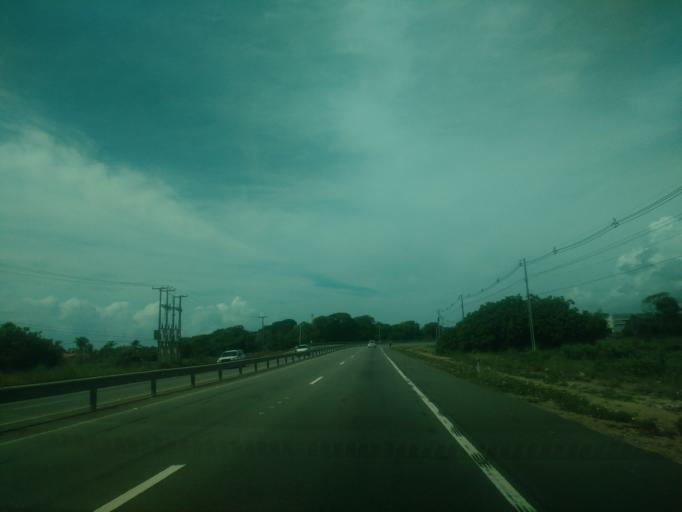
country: BR
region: Alagoas
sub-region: Marechal Deodoro
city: Marechal Deodoro
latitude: -9.7624
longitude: -35.8448
